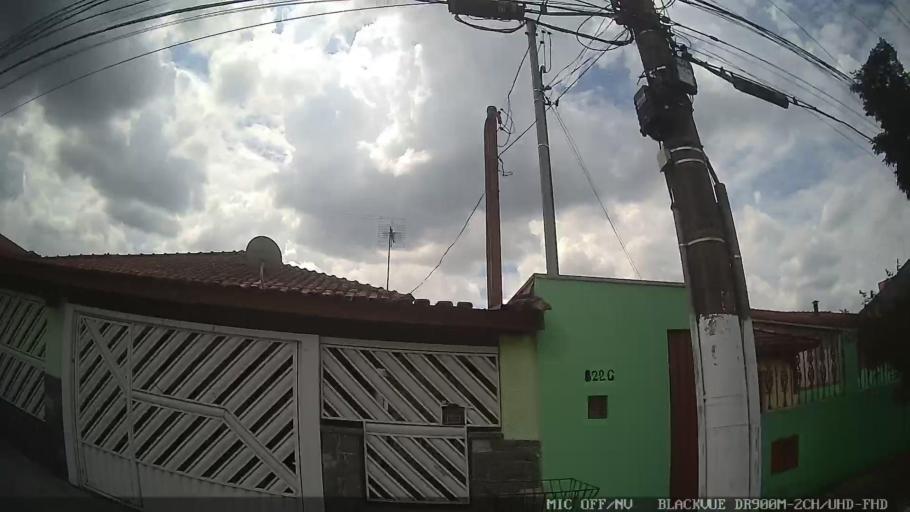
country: BR
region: Sao Paulo
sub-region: Ribeirao Pires
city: Ribeirao Pires
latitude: -23.7155
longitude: -46.4261
